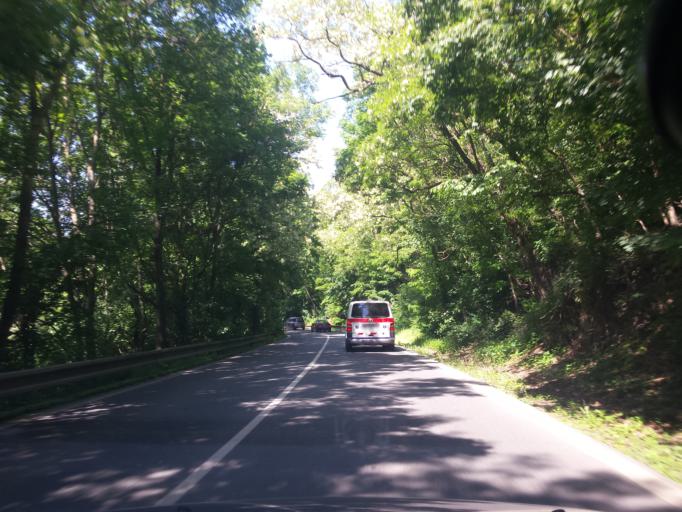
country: CZ
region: Central Bohemia
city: Horomerice
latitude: 50.1107
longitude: 14.3542
